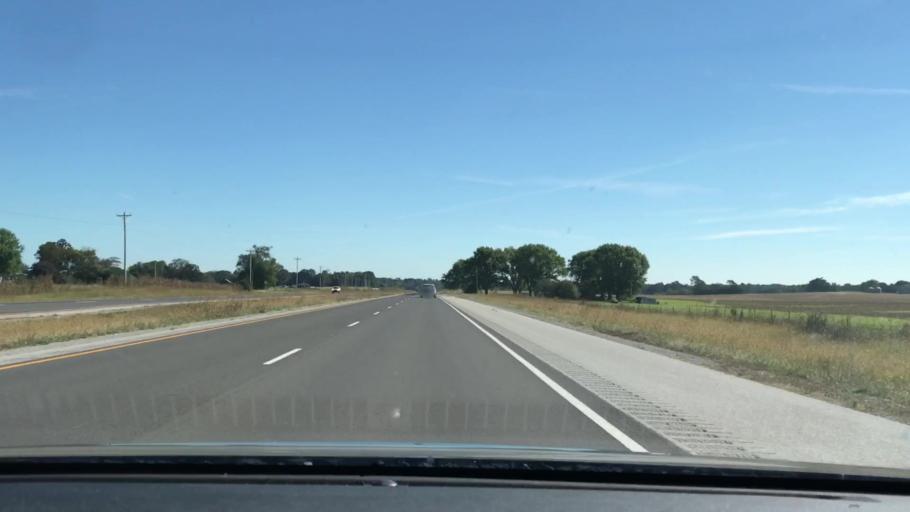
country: US
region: Kentucky
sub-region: Todd County
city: Elkton
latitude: 36.8125
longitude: -87.0294
